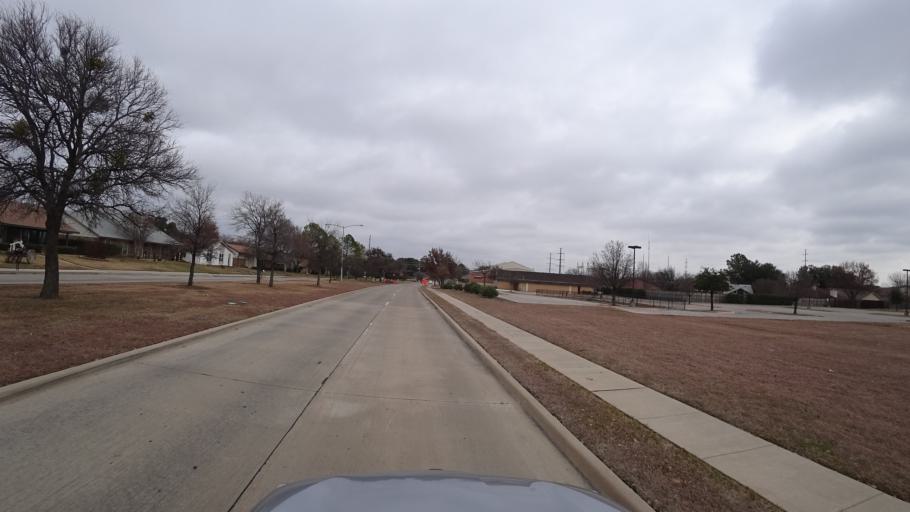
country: US
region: Texas
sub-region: Denton County
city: Highland Village
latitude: 33.0490
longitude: -97.0380
